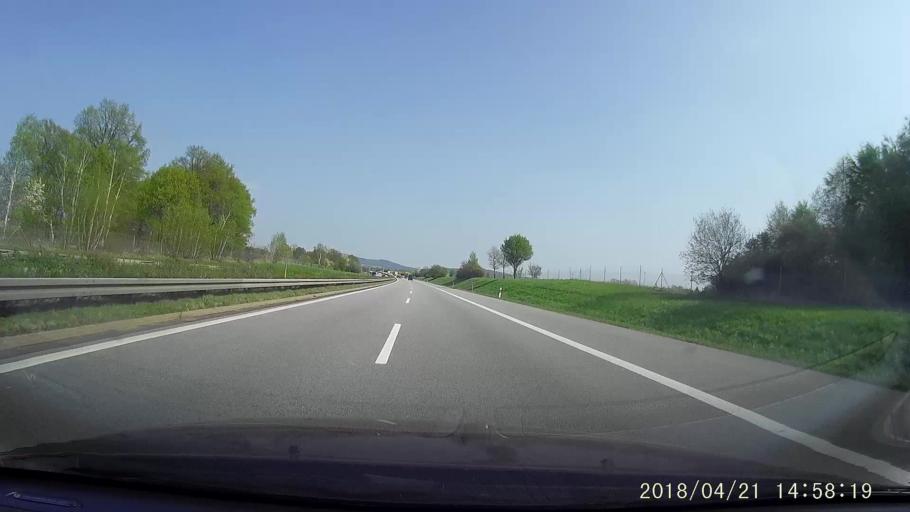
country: DE
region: Saxony
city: Weissenberg
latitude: 51.2101
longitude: 14.7308
